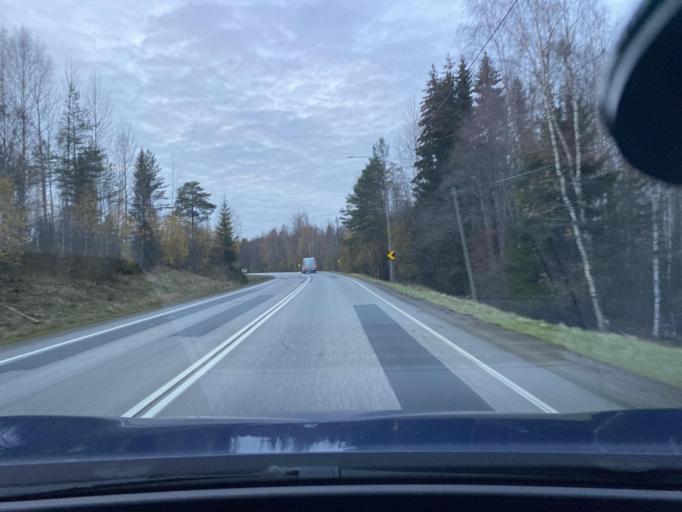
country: FI
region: Uusimaa
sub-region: Helsinki
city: Vihti
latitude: 60.3274
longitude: 24.2138
